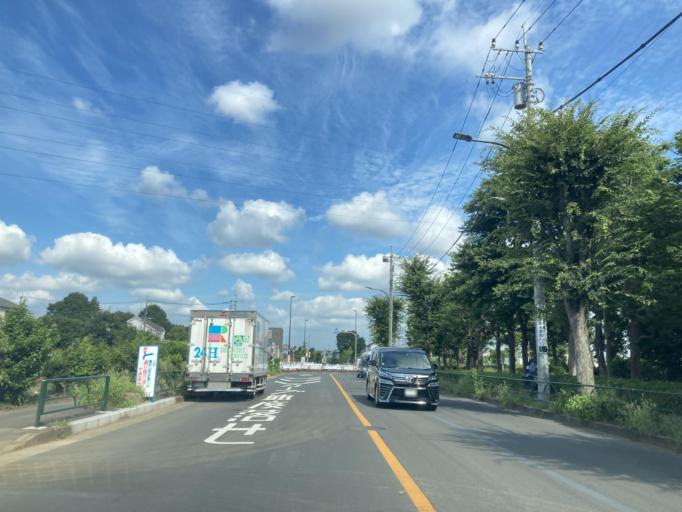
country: JP
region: Tokyo
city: Higashimurayama-shi
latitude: 35.7500
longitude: 139.4958
